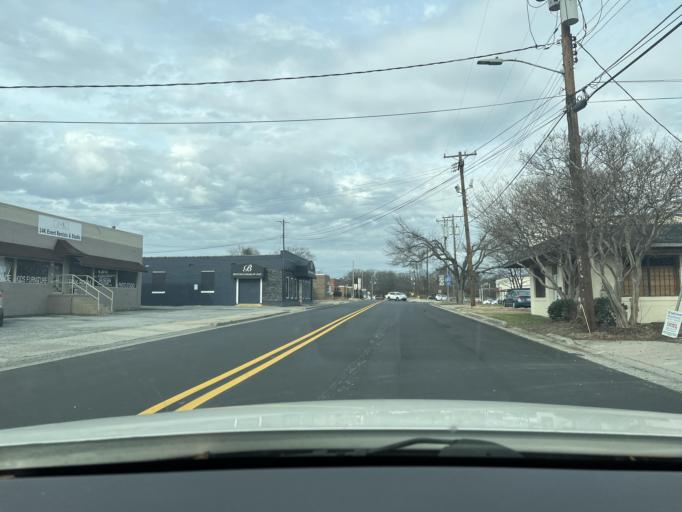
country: US
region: North Carolina
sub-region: Guilford County
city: Greensboro
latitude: 36.0854
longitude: -79.7683
